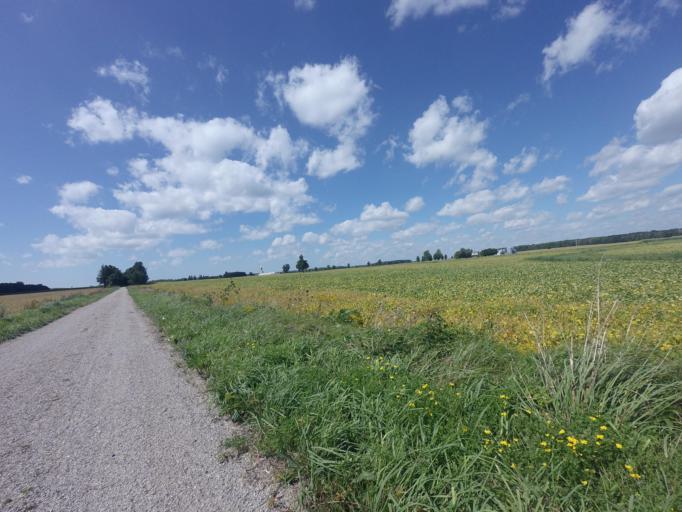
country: CA
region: Ontario
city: Huron East
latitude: 43.6657
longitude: -81.2644
